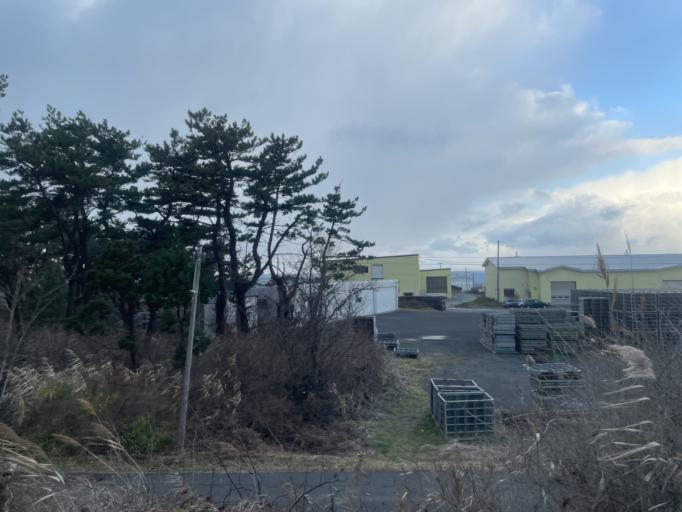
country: JP
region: Aomori
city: Mutsu
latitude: 41.0884
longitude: 141.2497
